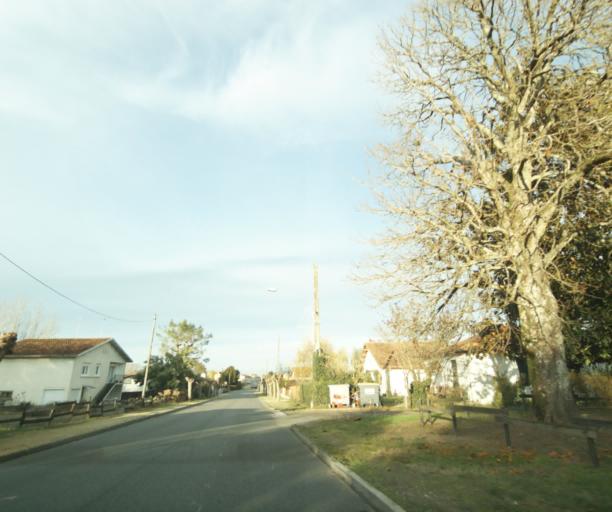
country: FR
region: Aquitaine
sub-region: Departement des Landes
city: Gabarret
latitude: 43.9811
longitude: 0.0082
